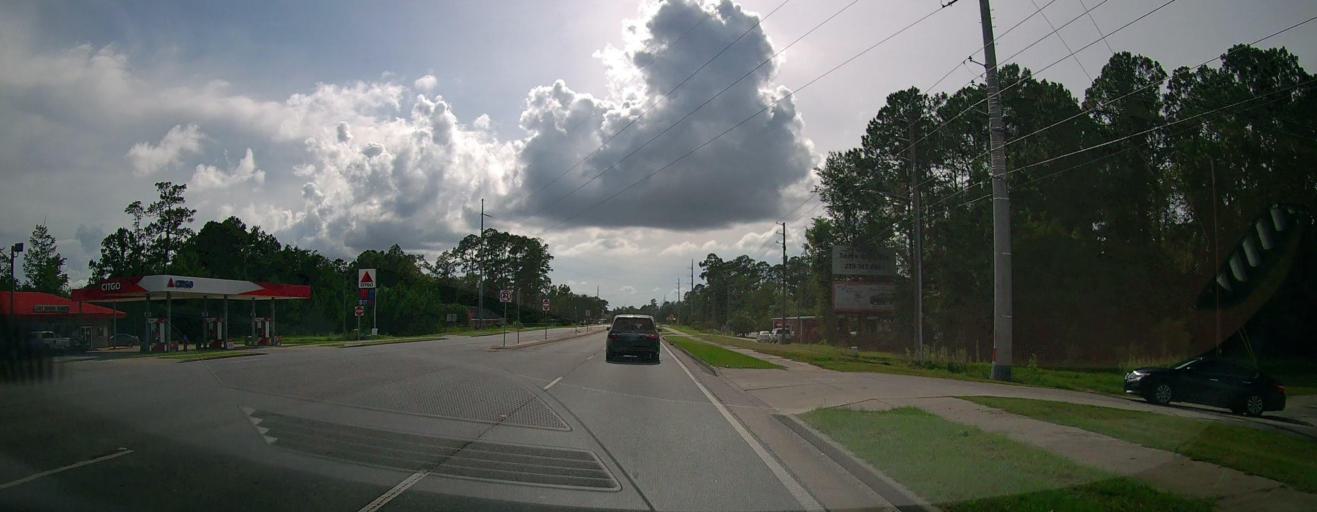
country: US
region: Georgia
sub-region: Wayne County
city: Jesup
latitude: 31.6047
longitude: -81.9088
